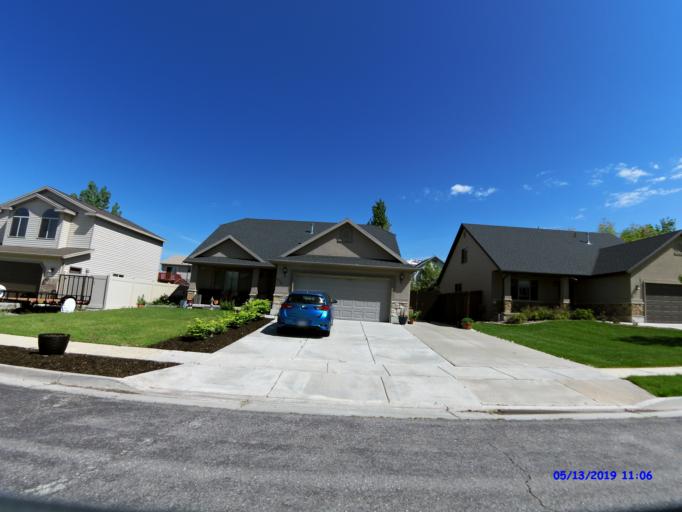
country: US
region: Utah
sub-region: Weber County
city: Harrisville
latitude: 41.2780
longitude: -111.9650
